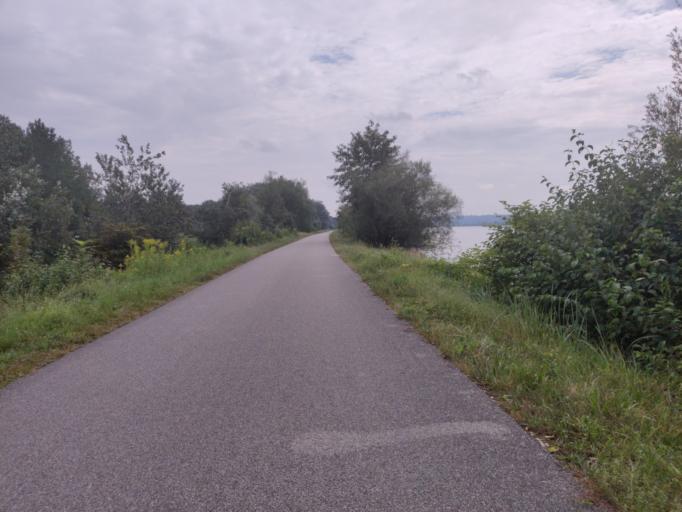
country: AT
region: Upper Austria
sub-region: Politischer Bezirk Perg
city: Perg
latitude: 48.1931
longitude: 14.6212
